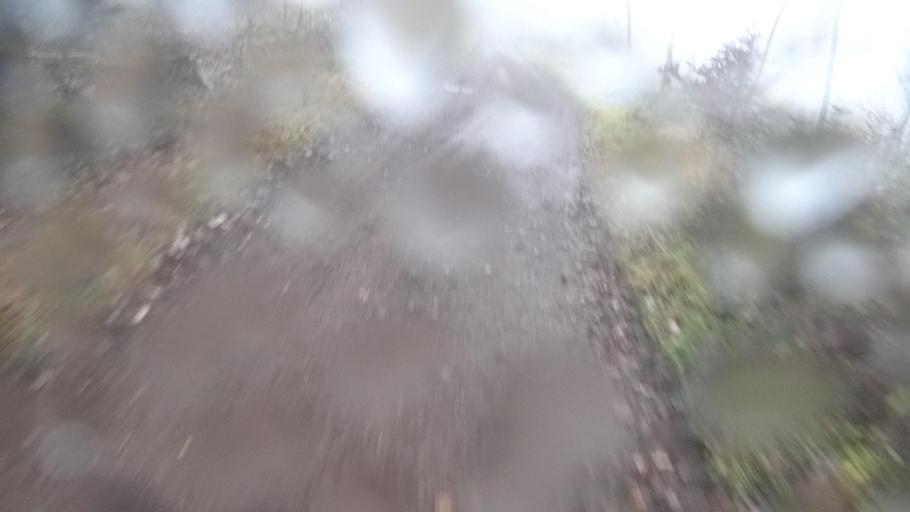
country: DE
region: Rheinland-Pfalz
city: Karbach
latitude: 50.1785
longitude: 7.6059
